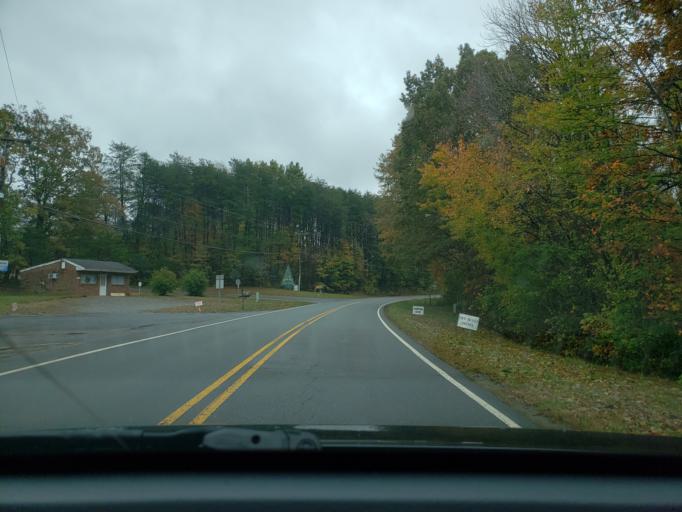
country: US
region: North Carolina
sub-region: Stokes County
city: Walnut Cove
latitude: 36.3519
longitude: -80.1554
